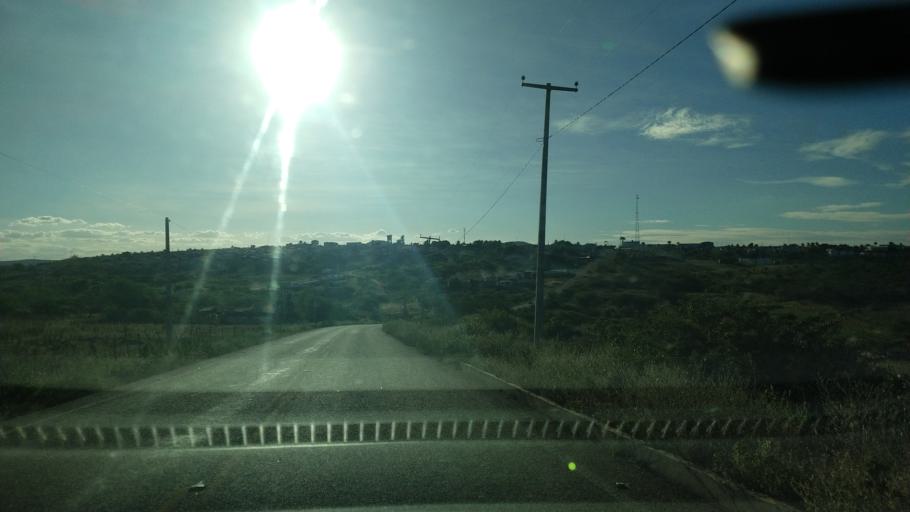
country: BR
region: Rio Grande do Norte
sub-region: Tangara
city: Tangara
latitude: -6.2076
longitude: -35.7947
